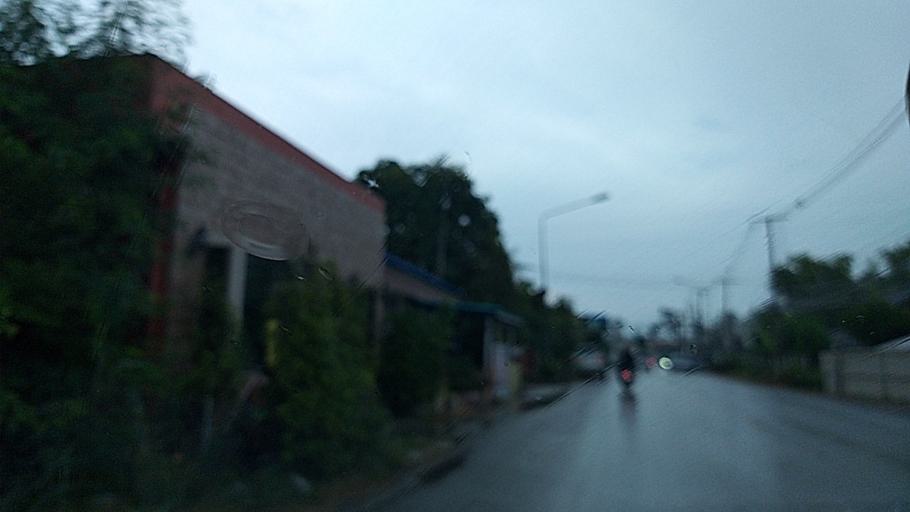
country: TH
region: Phra Nakhon Si Ayutthaya
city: Phra Nakhon Si Ayutthaya
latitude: 14.3483
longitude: 100.5423
